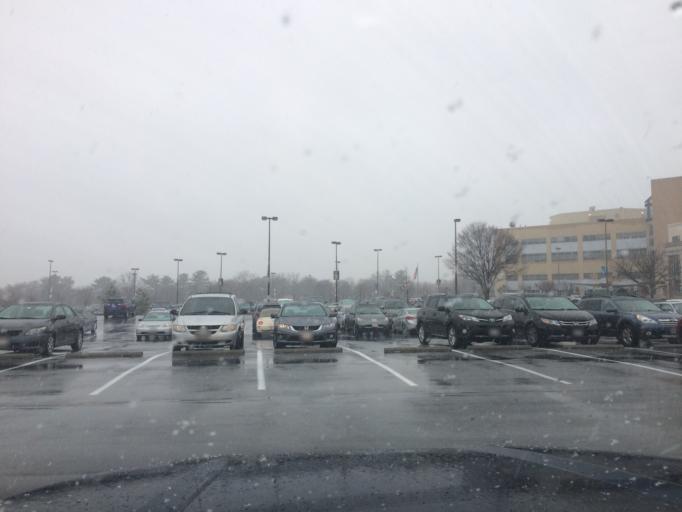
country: US
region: Maryland
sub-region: Howard County
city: Riverside
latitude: 39.2135
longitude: -76.8841
